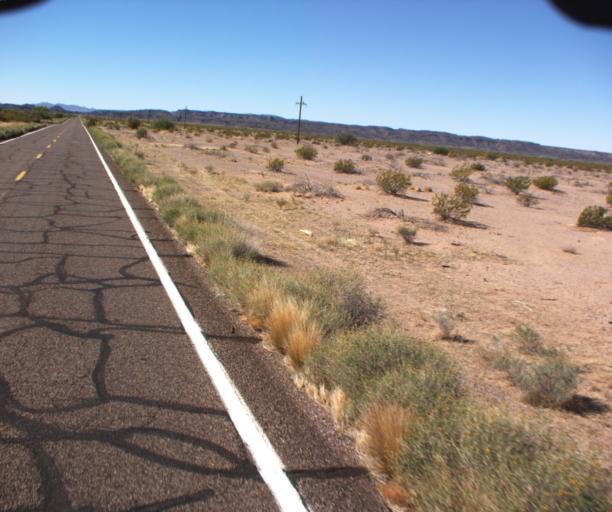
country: US
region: Arizona
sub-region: Pima County
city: Ajo
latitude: 32.6103
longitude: -112.8686
